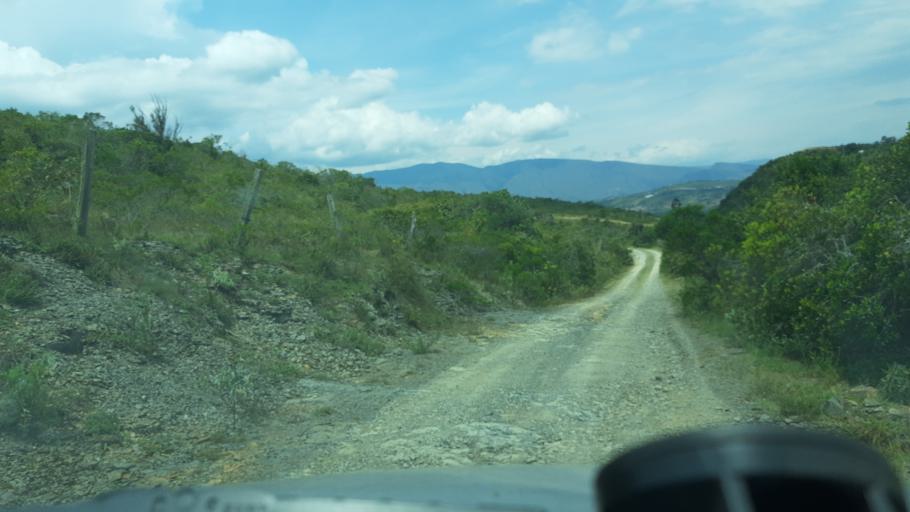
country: CO
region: Boyaca
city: Santa Sofia
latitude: 5.7016
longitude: -73.5807
